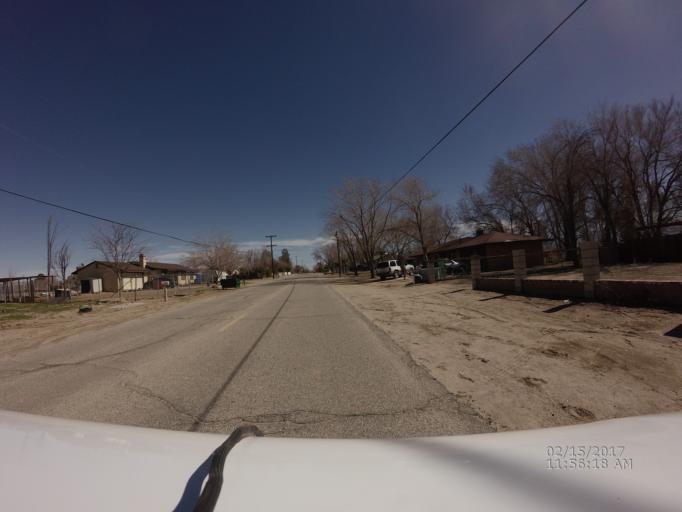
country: US
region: California
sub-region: Los Angeles County
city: Littlerock
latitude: 34.5743
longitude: -117.9550
